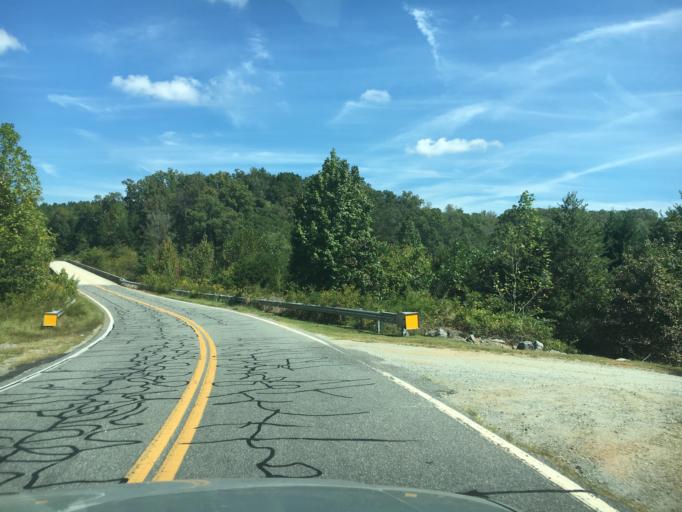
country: US
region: North Carolina
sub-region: Rutherford County
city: Forest City
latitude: 35.2254
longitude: -81.9321
